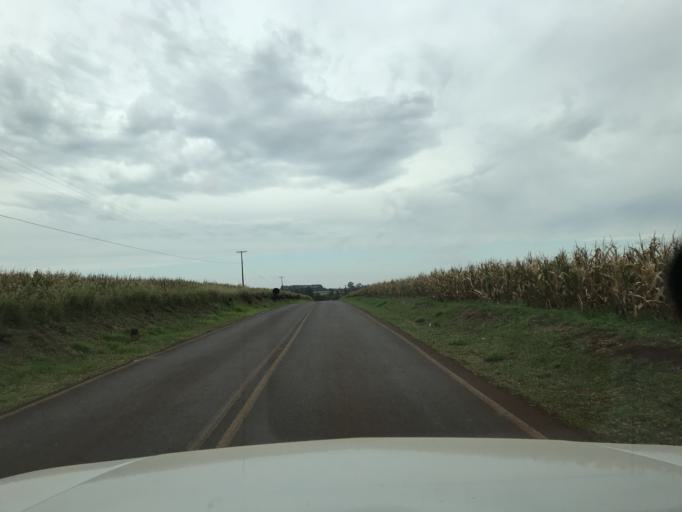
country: BR
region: Parana
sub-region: Marechal Candido Rondon
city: Marechal Candido Rondon
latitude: -24.4519
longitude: -53.9292
